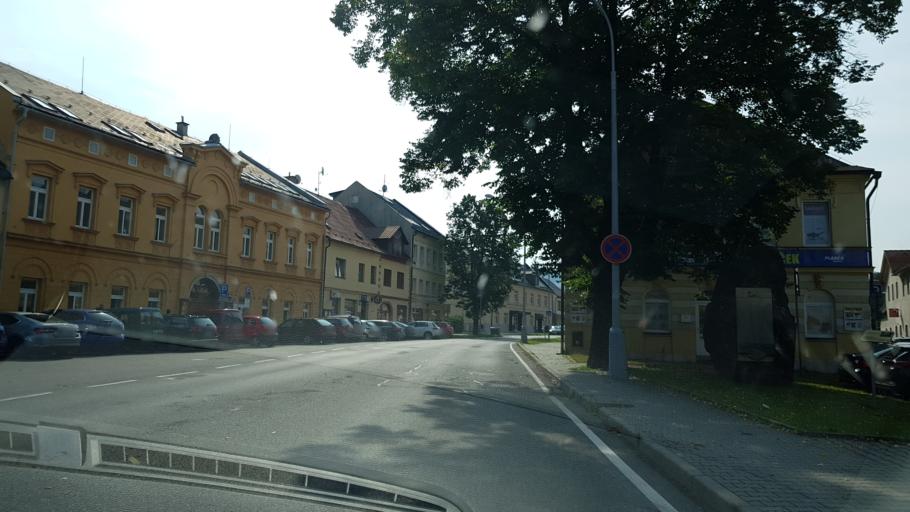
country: CZ
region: Olomoucky
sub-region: Okres Jesenik
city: Jesenik
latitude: 50.2267
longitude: 17.2055
